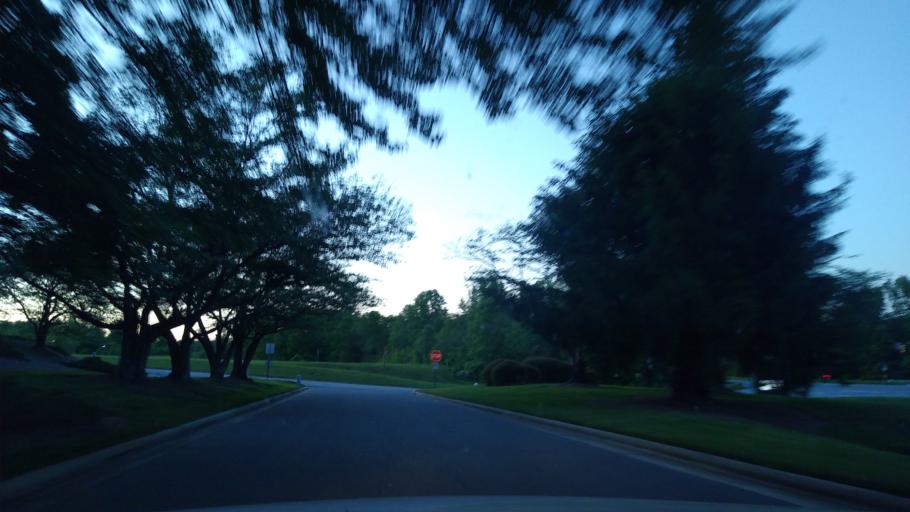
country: US
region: North Carolina
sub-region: Guilford County
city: Oak Ridge
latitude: 36.0853
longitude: -79.9630
